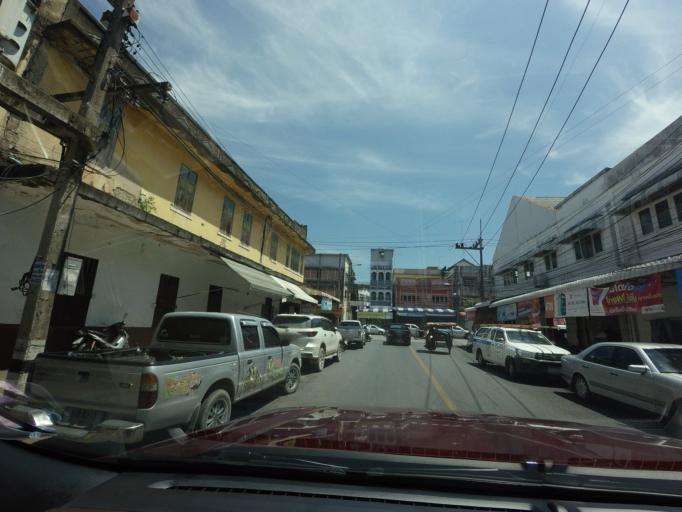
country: TH
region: Yala
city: Yala
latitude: 6.5591
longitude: 101.2922
